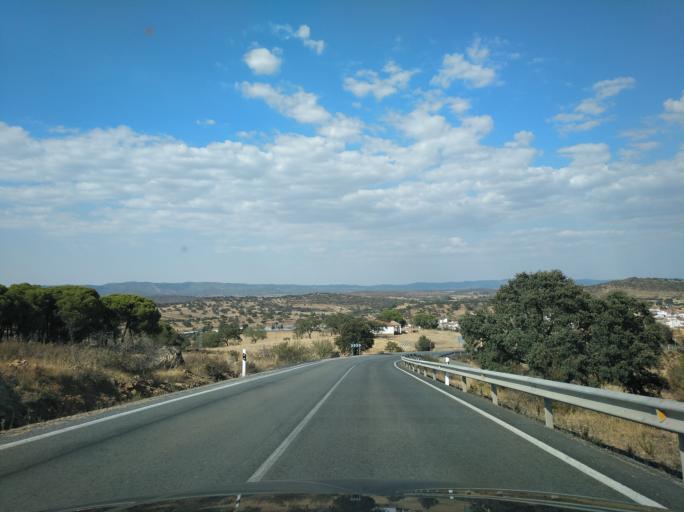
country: ES
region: Andalusia
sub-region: Provincia de Huelva
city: Cabezas Rubias
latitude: 37.7231
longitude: -7.0924
